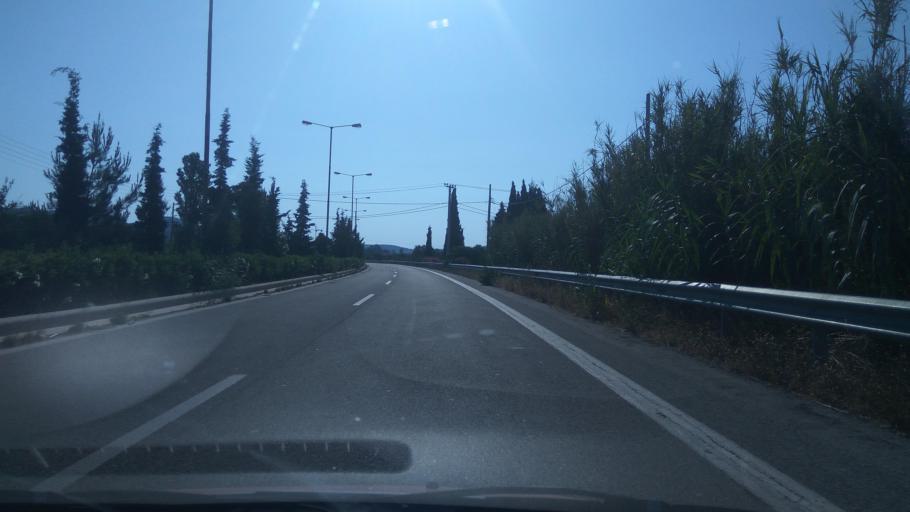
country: GR
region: Attica
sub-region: Nomarchia Anatolikis Attikis
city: Keratea
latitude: 37.7998
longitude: 24.0039
